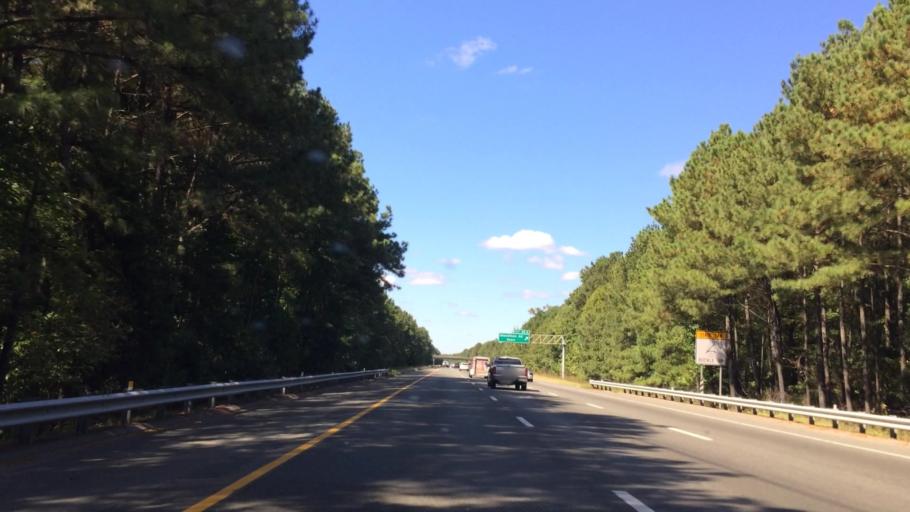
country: US
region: Virginia
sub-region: Henrico County
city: Glen Allen
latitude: 37.6638
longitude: -77.4783
